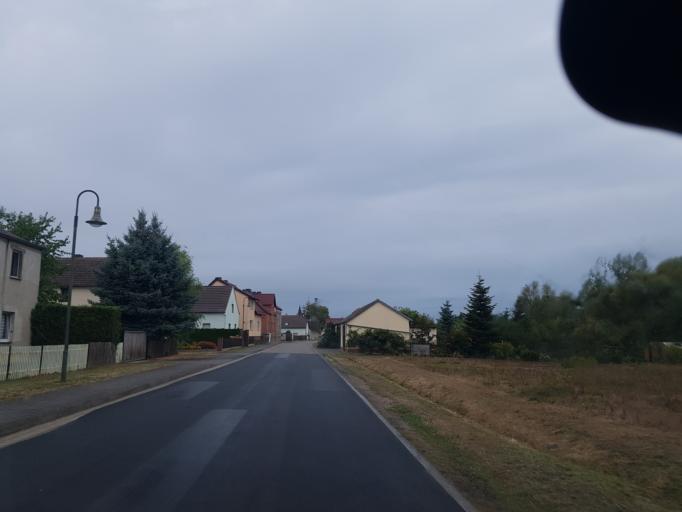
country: DE
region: Saxony-Anhalt
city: Elster
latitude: 51.7973
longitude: 12.8709
